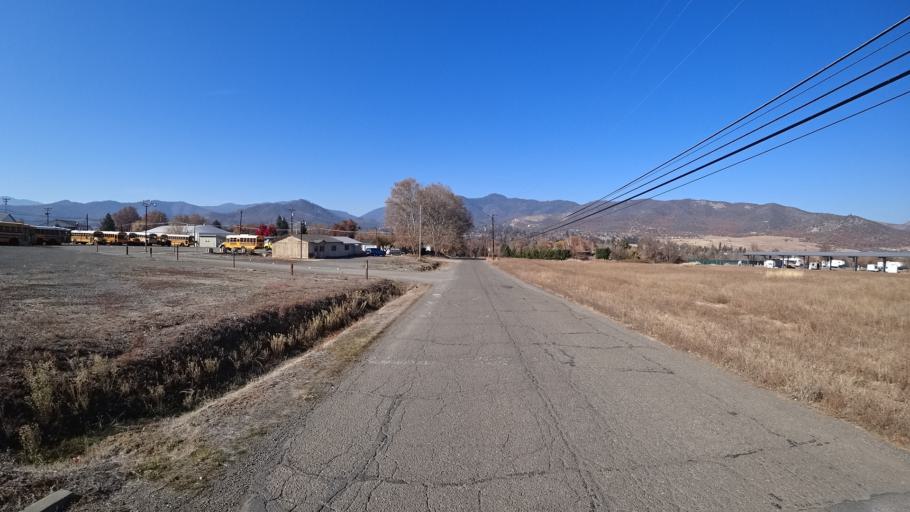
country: US
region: California
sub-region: Siskiyou County
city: Yreka
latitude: 41.7349
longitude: -122.6269
